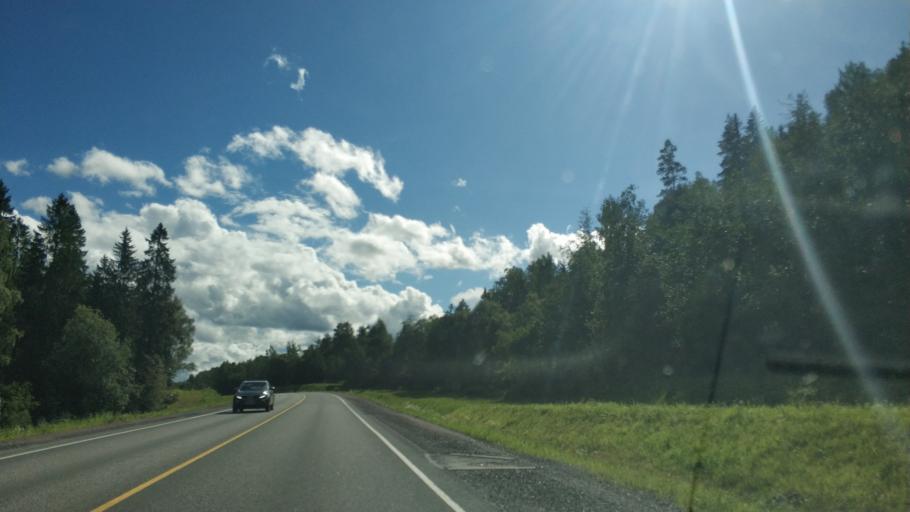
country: RU
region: Republic of Karelia
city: Ruskeala
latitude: 61.8975
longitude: 30.6366
